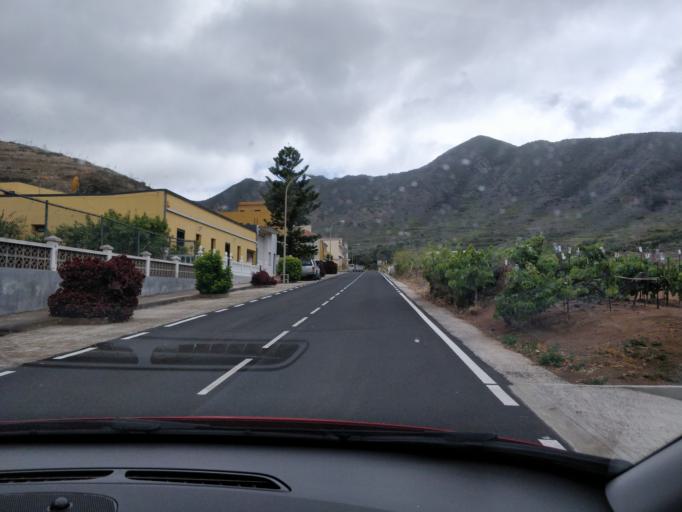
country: ES
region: Canary Islands
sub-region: Provincia de Santa Cruz de Tenerife
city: Tanque
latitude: 28.3435
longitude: -16.8477
